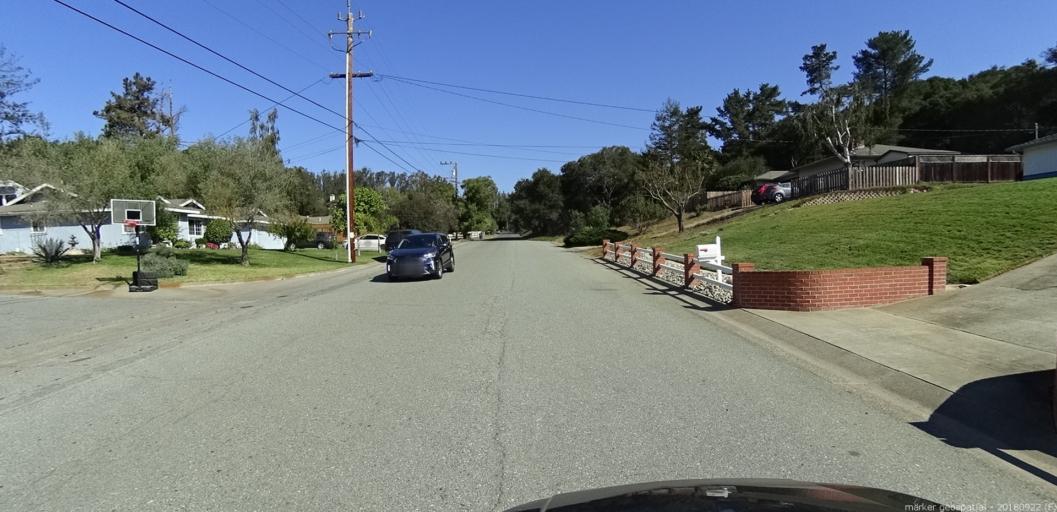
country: US
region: California
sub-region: Monterey County
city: Prunedale
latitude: 36.8151
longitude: -121.6547
